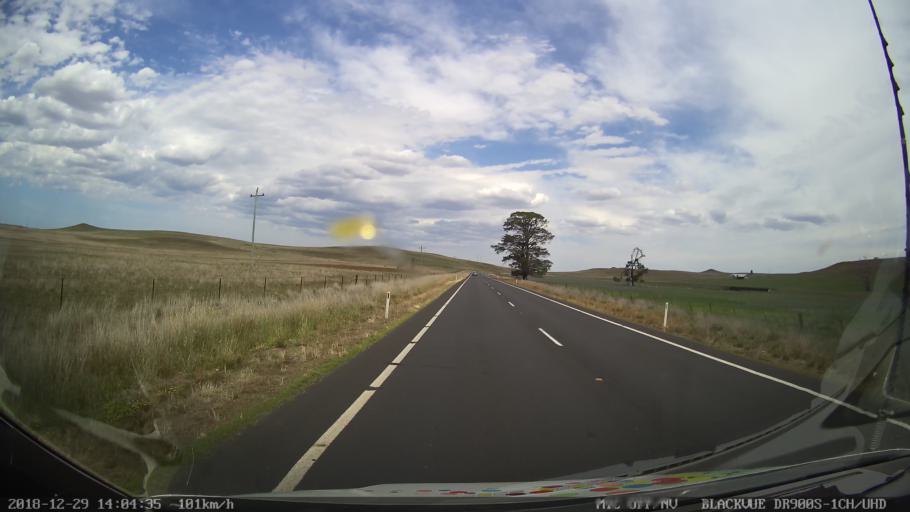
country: AU
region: New South Wales
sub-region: Cooma-Monaro
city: Cooma
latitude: -36.3183
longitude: 149.1875
